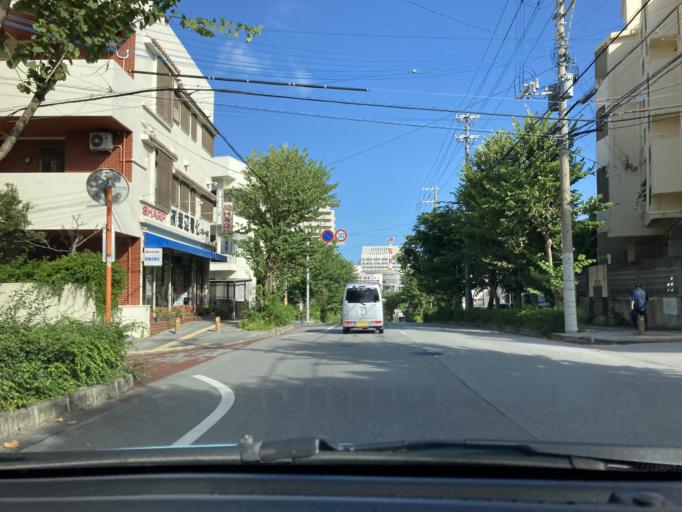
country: JP
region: Okinawa
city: Naha-shi
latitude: 26.2075
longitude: 127.6834
